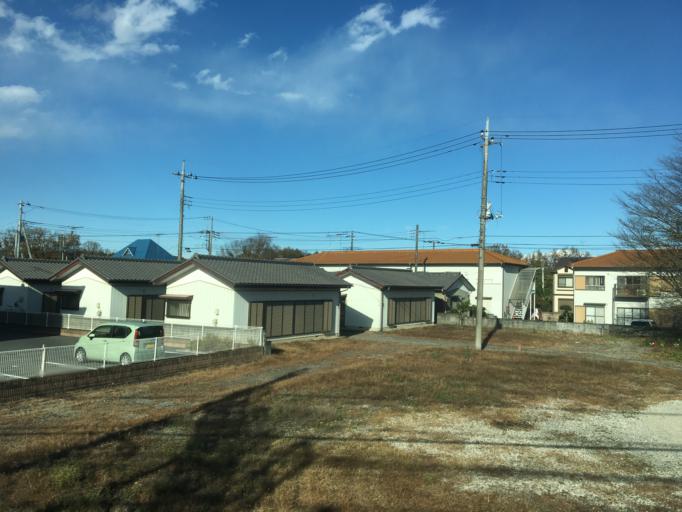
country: JP
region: Saitama
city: Kumagaya
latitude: 36.0468
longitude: 139.3683
